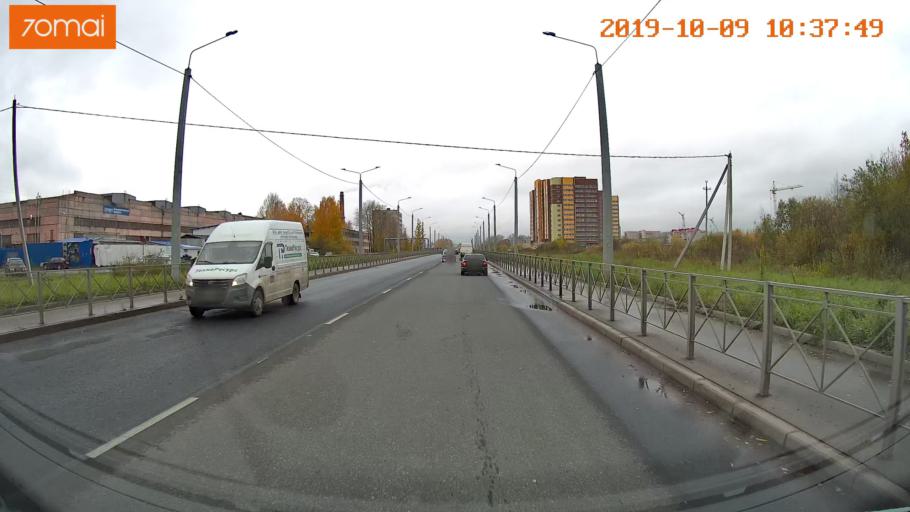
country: RU
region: Vologda
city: Vologda
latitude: 59.2356
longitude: 39.8554
